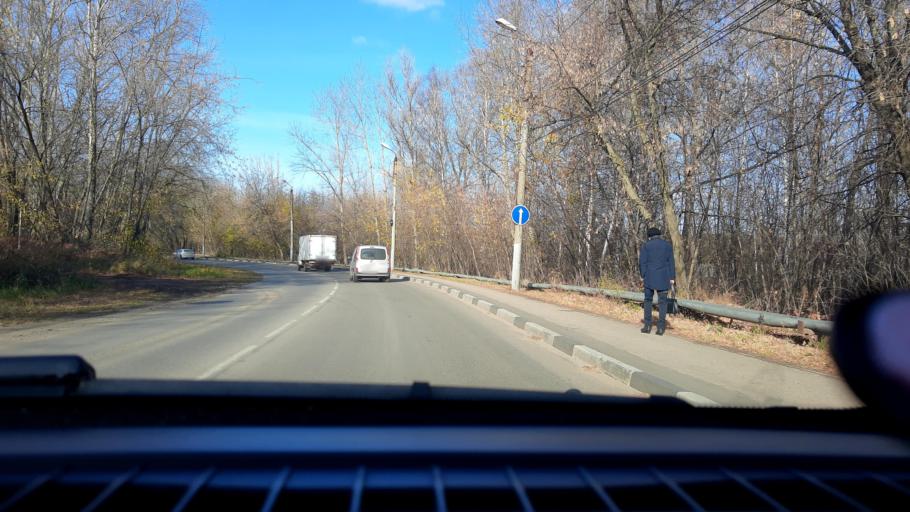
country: RU
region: Nizjnij Novgorod
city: Kstovo
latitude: 56.1606
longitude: 44.2063
